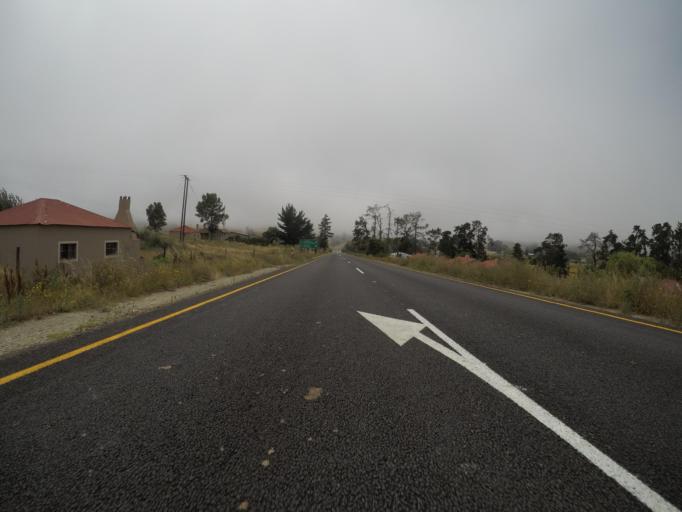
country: ZA
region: Western Cape
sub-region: Eden District Municipality
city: Knysna
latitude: -33.7260
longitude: 23.1614
